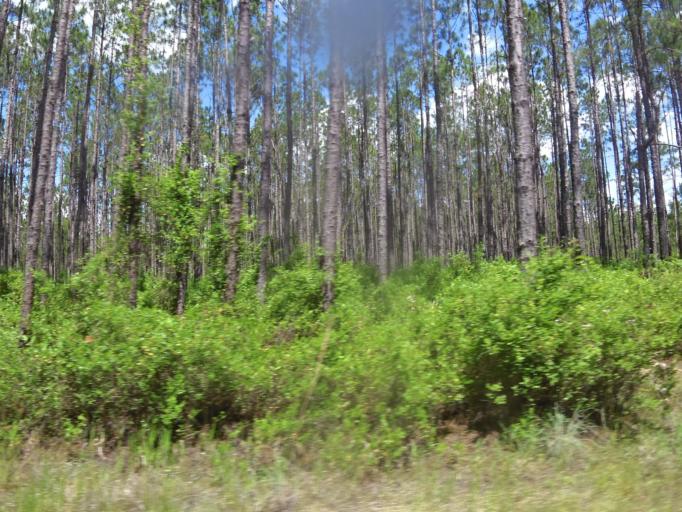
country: US
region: Florida
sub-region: Clay County
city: Asbury Lake
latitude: 29.8666
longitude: -81.8534
